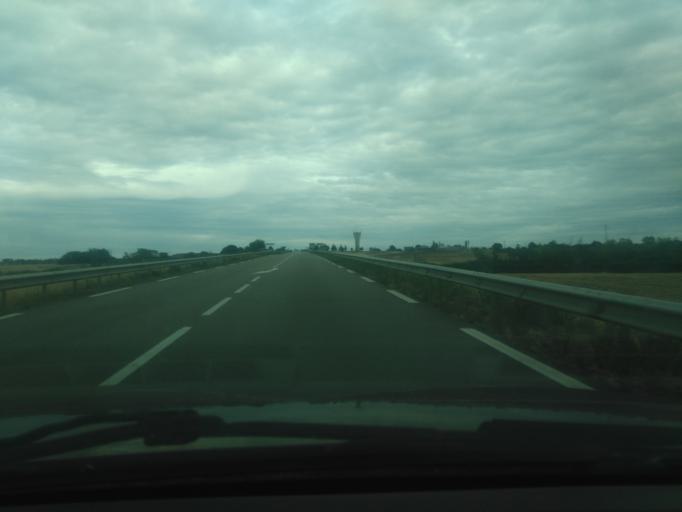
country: FR
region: Bourgogne
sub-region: Departement de la Nievre
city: Saint-Pierre-le-Moutier
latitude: 46.8024
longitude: 3.1109
